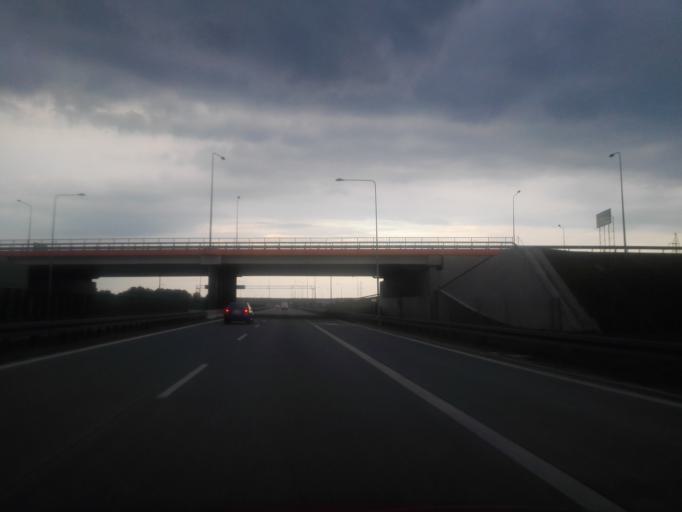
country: PL
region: Lodz Voivodeship
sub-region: Piotrkow Trybunalski
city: Piotrkow Trybunalski
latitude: 51.4436
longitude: 19.7223
